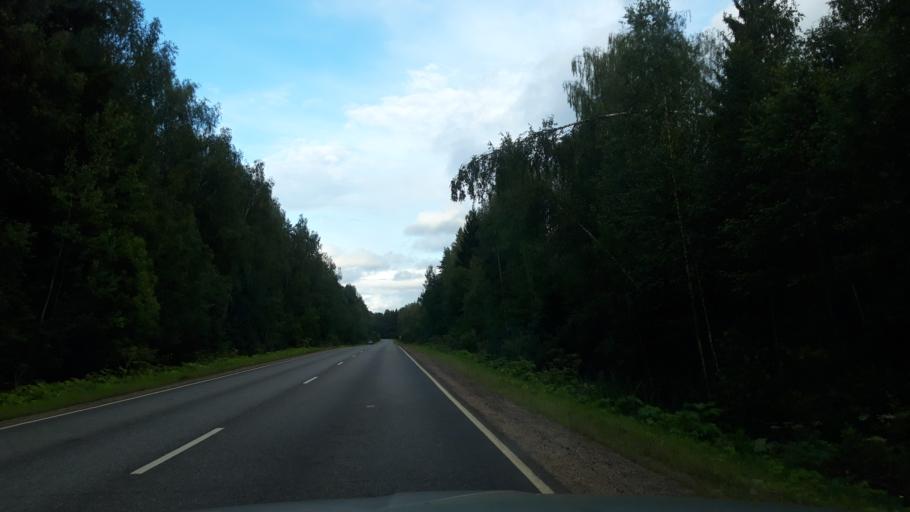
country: RU
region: Moskovskaya
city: Solnechnogorsk
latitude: 56.0946
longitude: 36.8884
